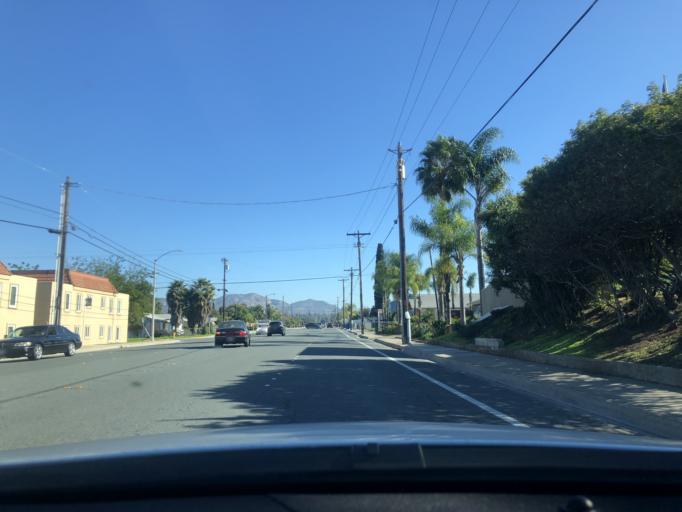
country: US
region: California
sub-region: San Diego County
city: Bostonia
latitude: 32.7876
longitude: -116.9422
